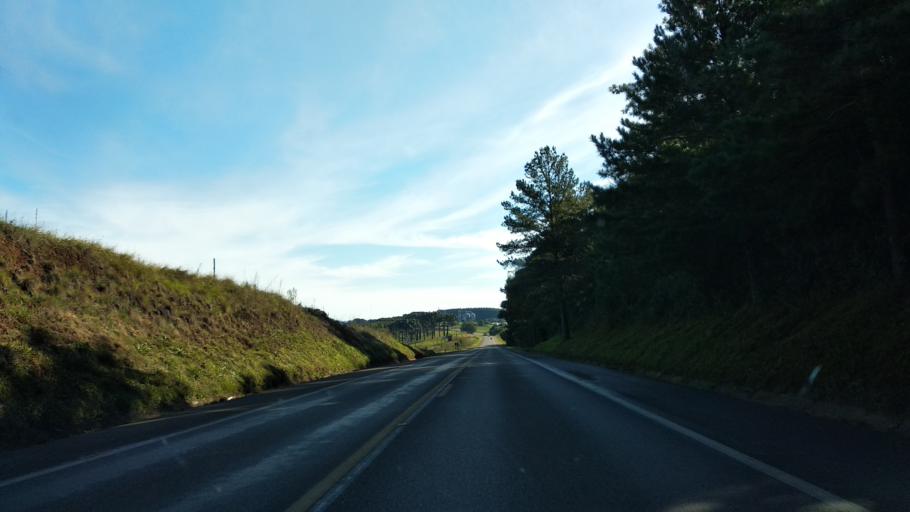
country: BR
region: Santa Catarina
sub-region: Celso Ramos
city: Celso Ramos
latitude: -27.5270
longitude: -51.3664
